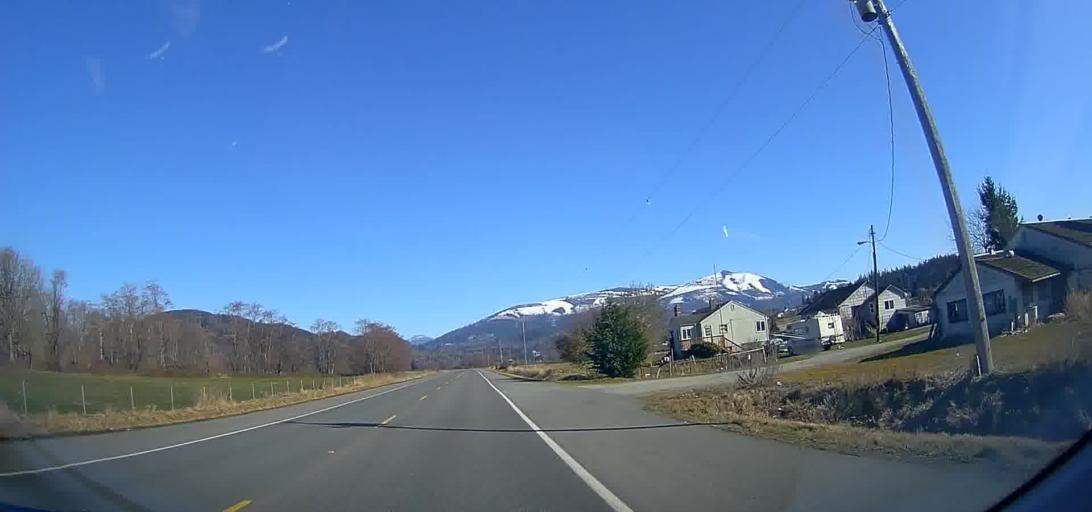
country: US
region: Washington
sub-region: Skagit County
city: Clear Lake
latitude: 48.4643
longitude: -122.2644
